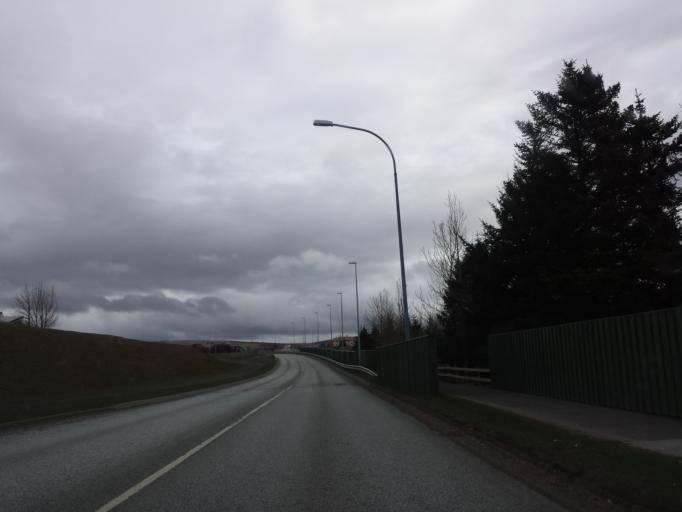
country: IS
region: Capital Region
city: Gardabaer
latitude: 64.0839
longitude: -21.9015
